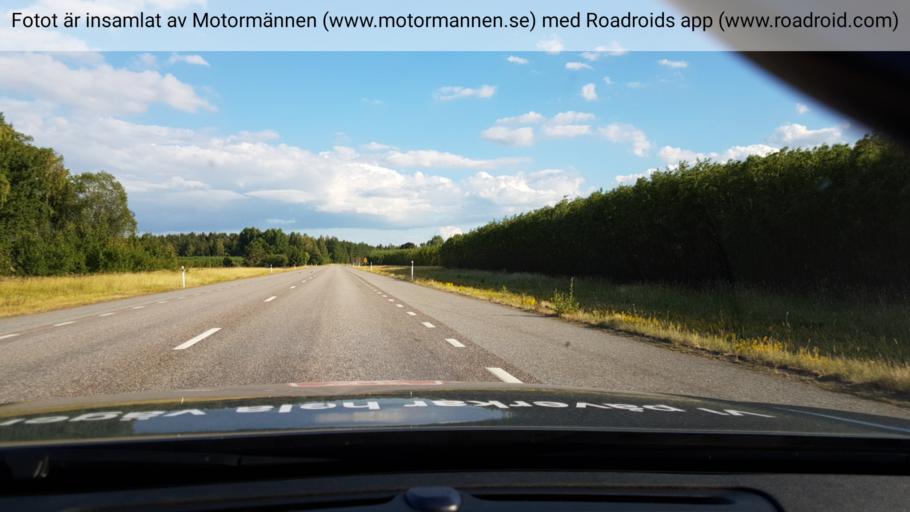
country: SE
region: Uppsala
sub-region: Heby Kommun
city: Morgongava
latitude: 59.8592
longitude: 16.9284
